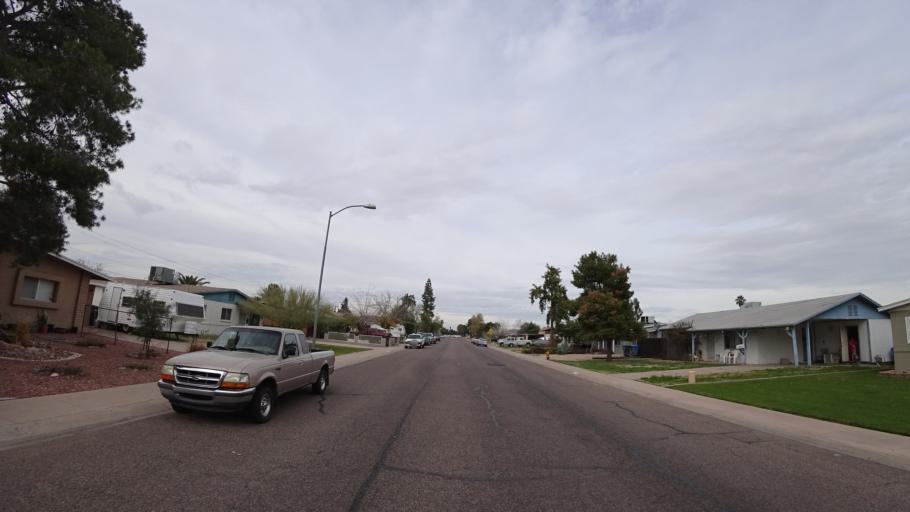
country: US
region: Arizona
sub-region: Maricopa County
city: Glendale
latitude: 33.6231
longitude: -112.1204
